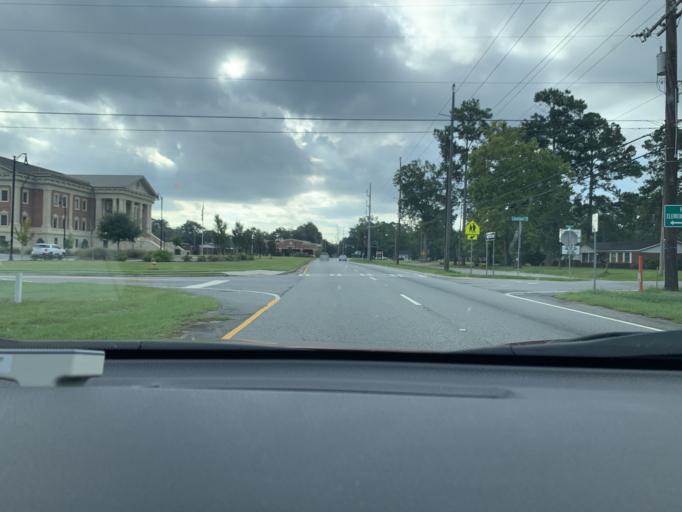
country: US
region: Georgia
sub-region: Chatham County
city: Pooler
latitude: 32.1159
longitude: -81.2517
